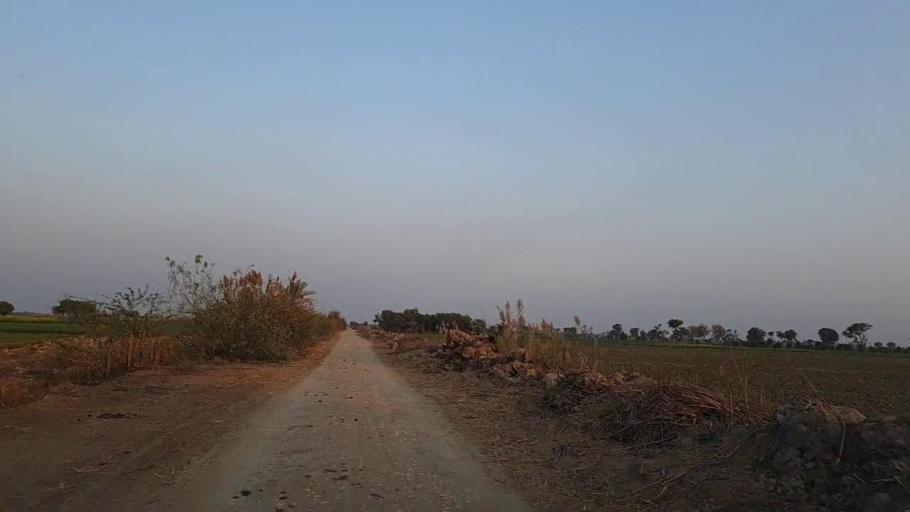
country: PK
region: Sindh
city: Jam Sahib
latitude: 26.3051
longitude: 68.5580
